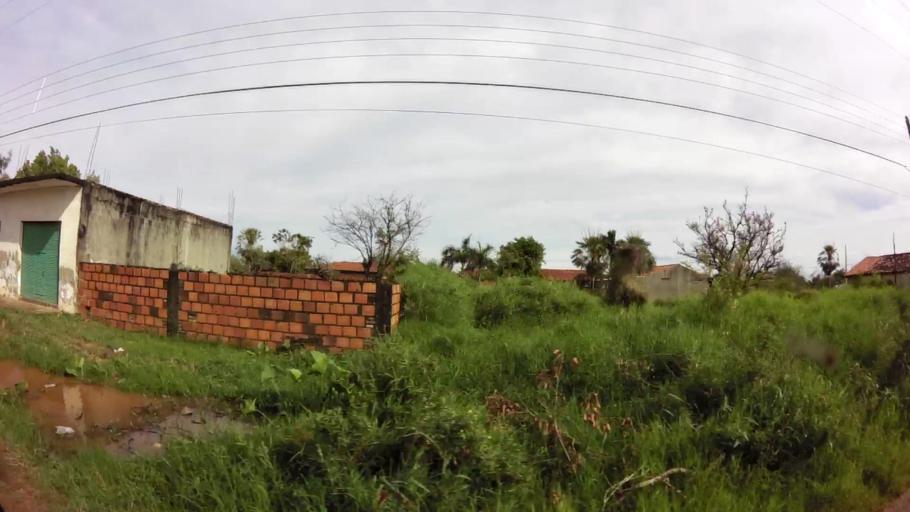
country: PY
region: Central
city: Limpio
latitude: -25.1776
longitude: -57.4954
